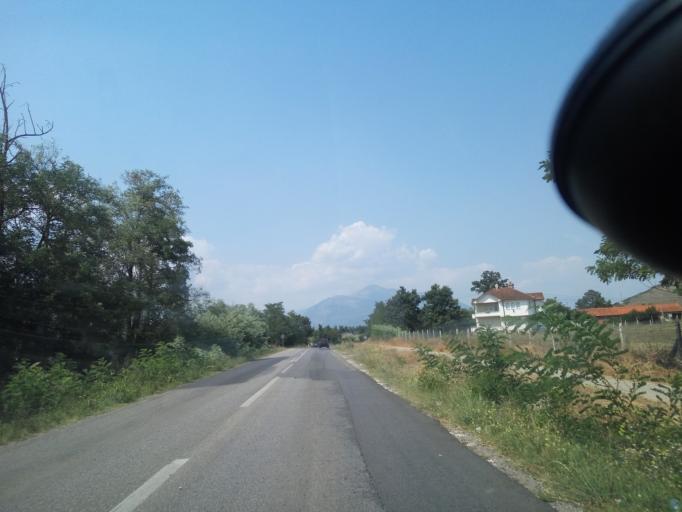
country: XK
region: Gjakova
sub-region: Komuna e Decanit
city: Gllogjan
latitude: 42.4622
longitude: 20.3490
